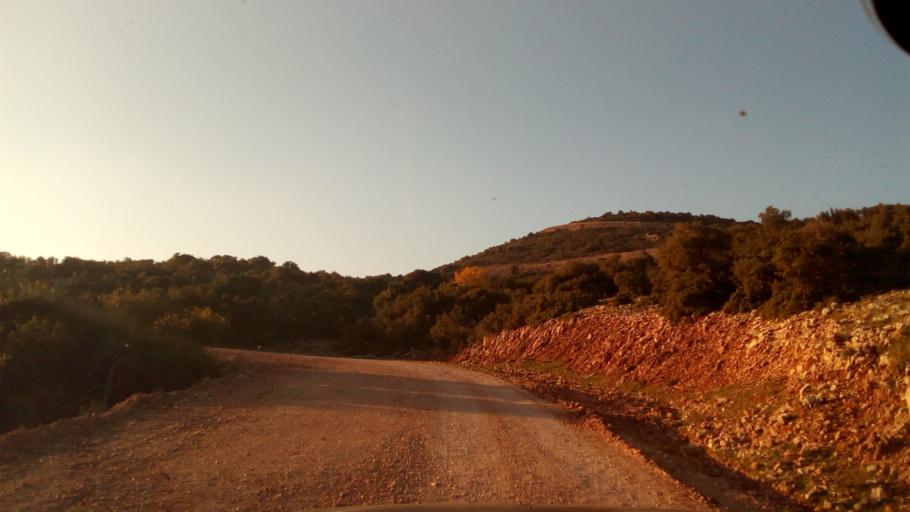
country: GR
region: West Greece
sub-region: Nomos Aitolias kai Akarnanias
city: Nafpaktos
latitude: 38.4313
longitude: 21.8542
